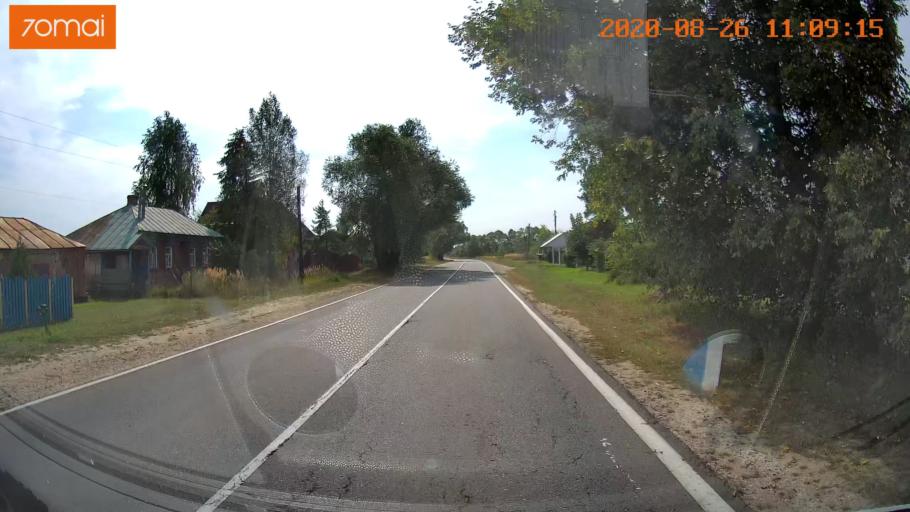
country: RU
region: Rjazan
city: Izhevskoye
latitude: 54.4933
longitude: 41.1235
